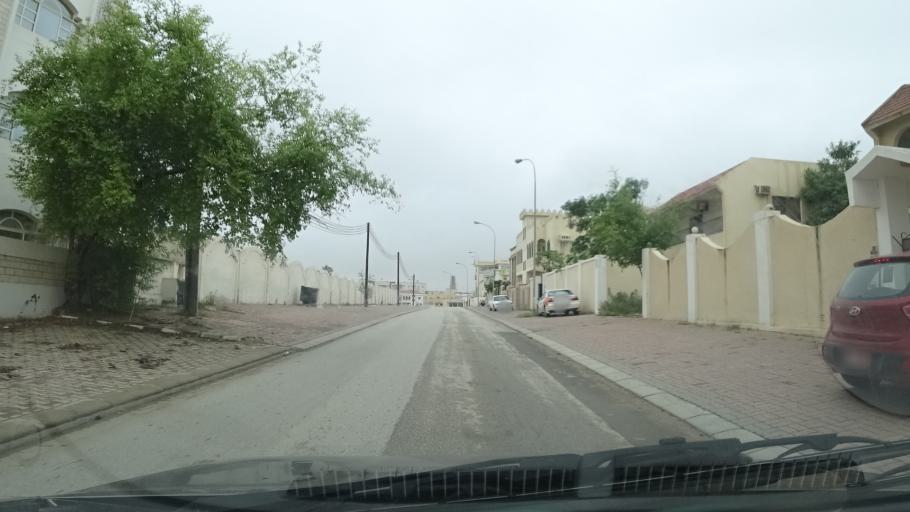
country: OM
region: Zufar
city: Salalah
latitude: 17.0179
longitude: 54.0710
